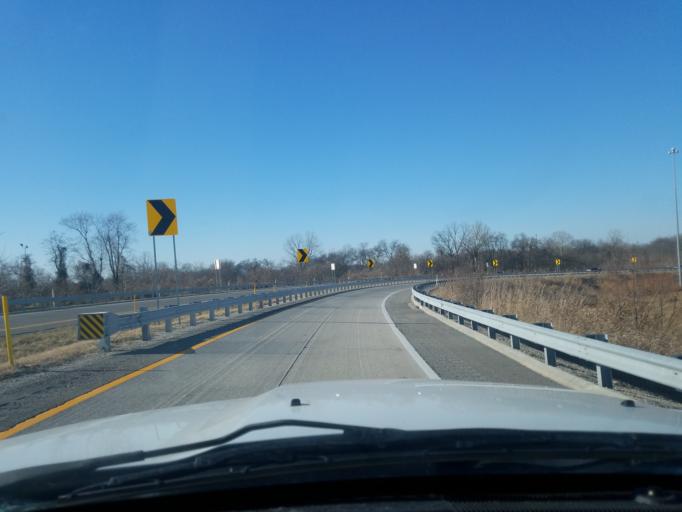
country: US
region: Kentucky
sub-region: Henderson County
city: Henderson
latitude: 37.8102
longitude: -87.5655
